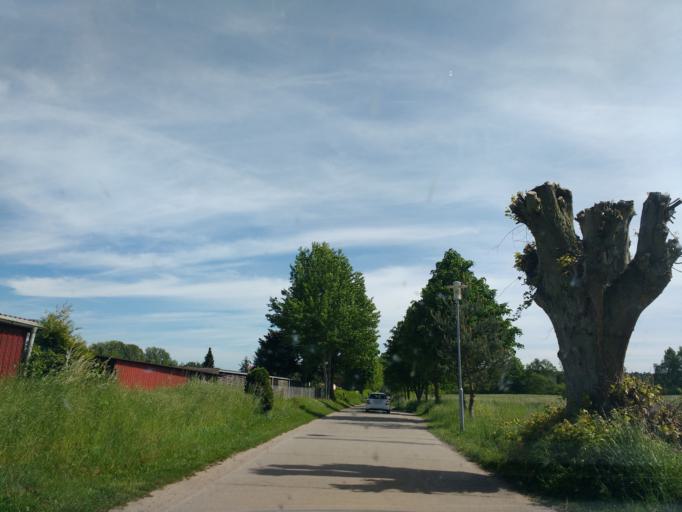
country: DE
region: Mecklenburg-Vorpommern
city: Neukloster
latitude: 53.8520
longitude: 11.6820
